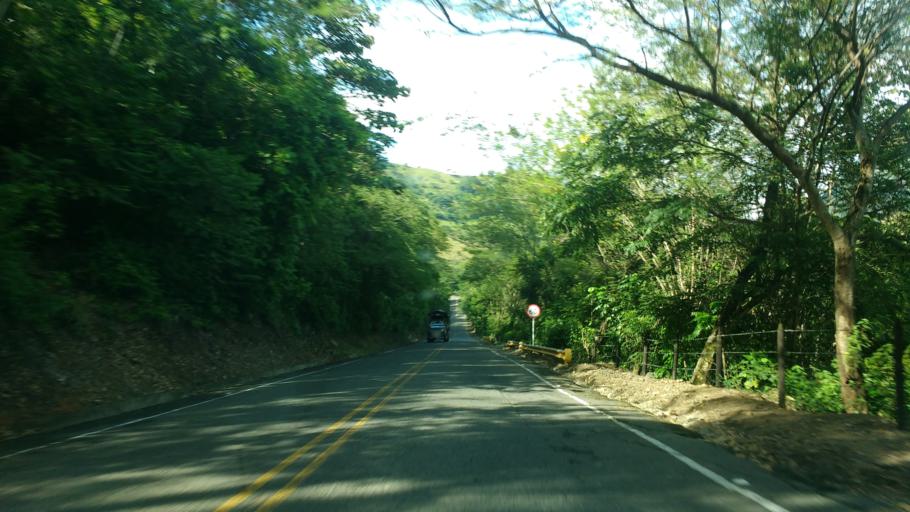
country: CO
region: Antioquia
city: Concordia
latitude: 6.0523
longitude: -75.8666
